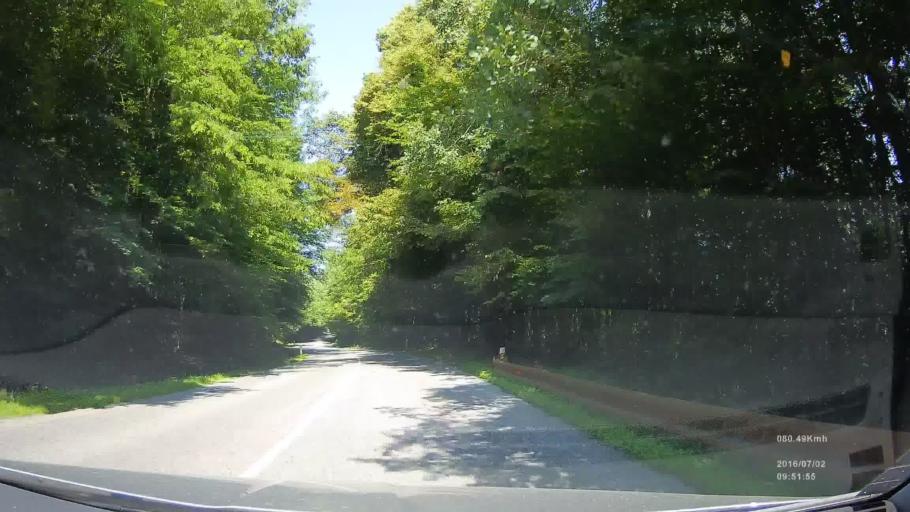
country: SK
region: Kosicky
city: Gelnica
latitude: 48.9069
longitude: 20.9692
